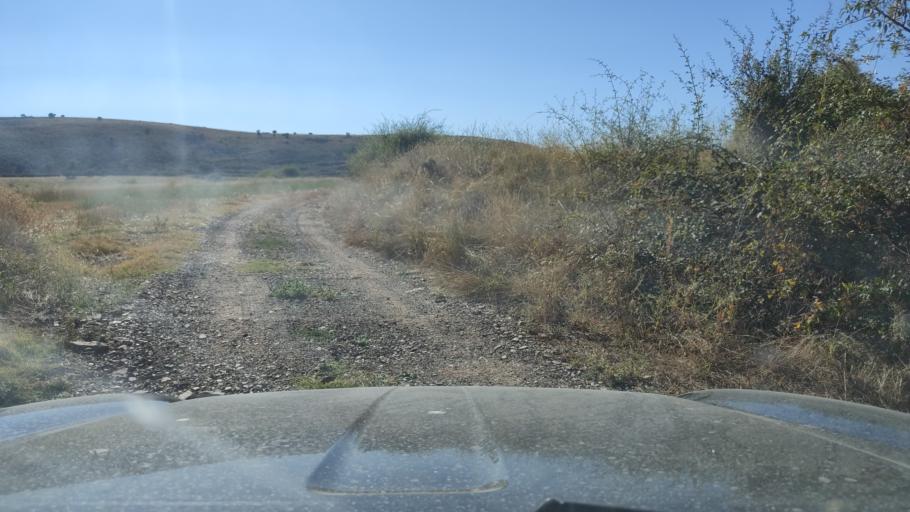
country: ES
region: Aragon
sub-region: Provincia de Teruel
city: Monforte de Moyuela
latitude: 41.0296
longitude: -1.0103
